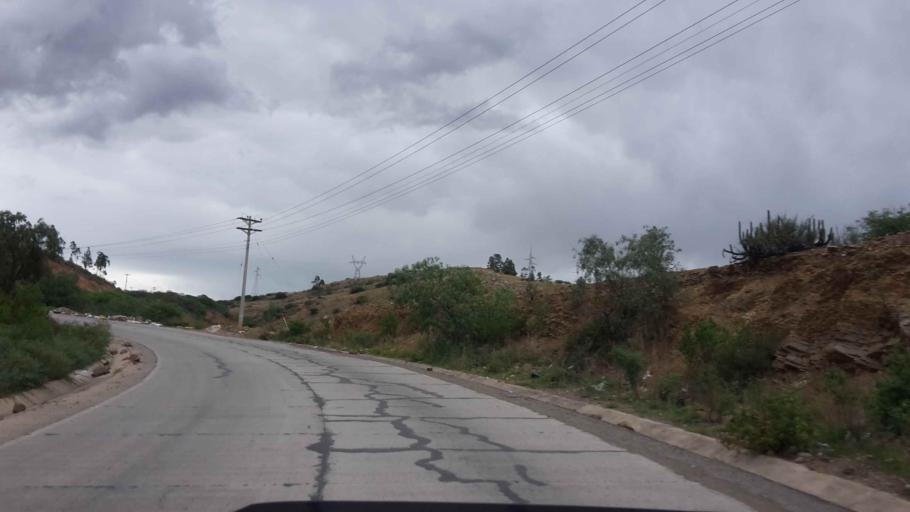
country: BO
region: Cochabamba
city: Cochabamba
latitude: -17.5316
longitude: -66.1982
